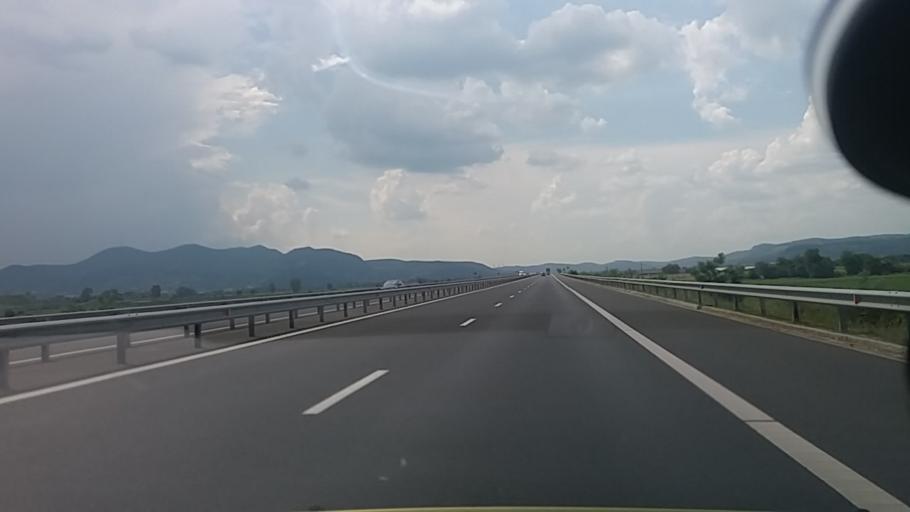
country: RO
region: Hunedoara
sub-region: Comuna Harau
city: Harau
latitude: 45.8904
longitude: 22.9636
